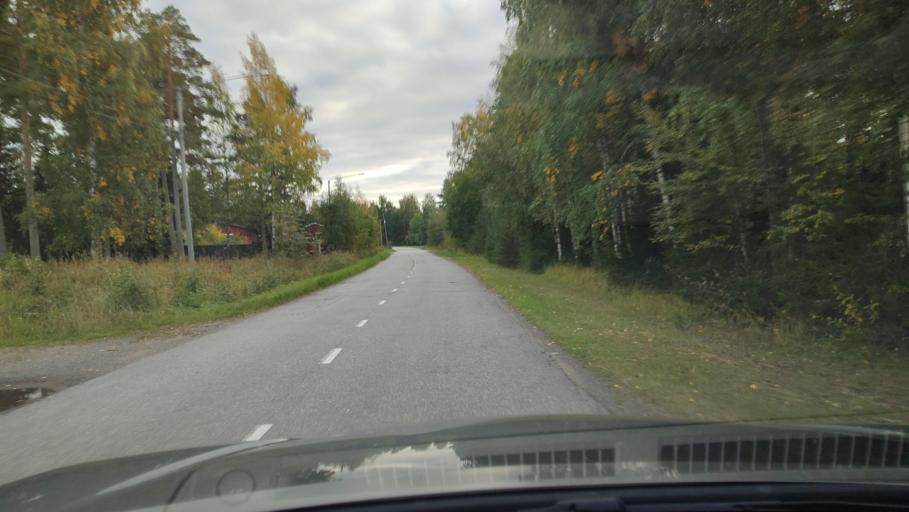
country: FI
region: Ostrobothnia
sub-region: Sydosterbotten
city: Kristinestad
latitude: 62.2612
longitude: 21.3845
